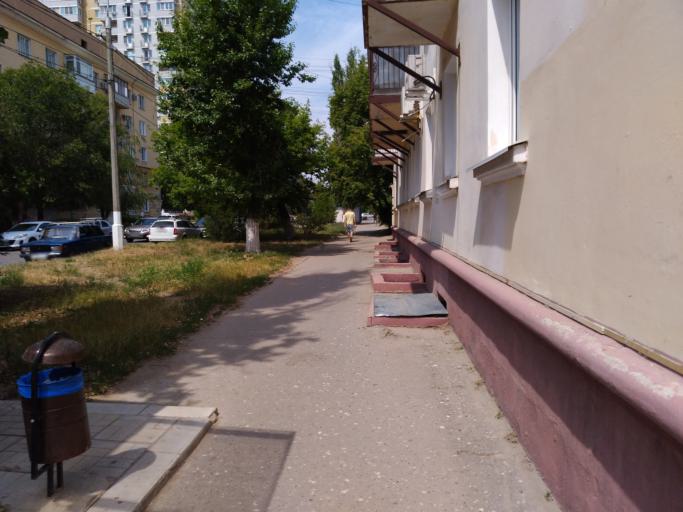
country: RU
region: Volgograd
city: Volgograd
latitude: 48.6969
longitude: 44.4953
